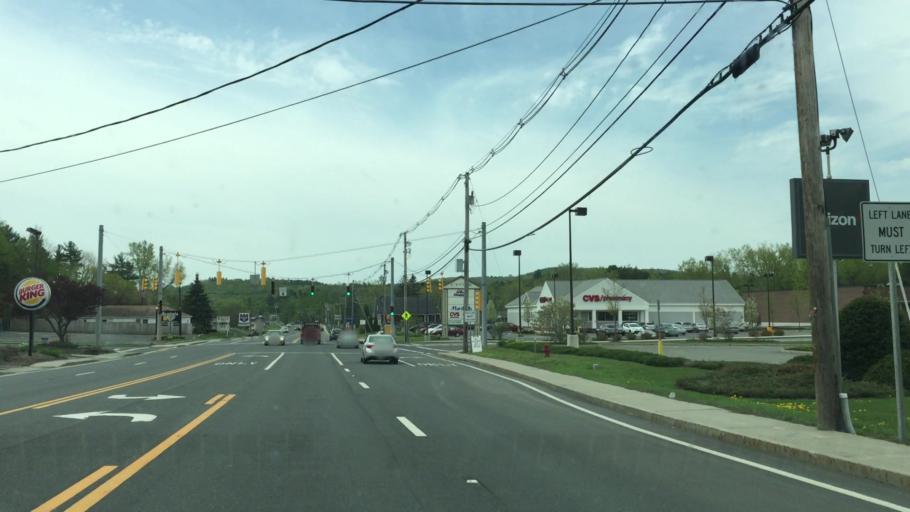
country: US
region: Massachusetts
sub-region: Berkshire County
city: Pittsfield
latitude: 42.4055
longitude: -73.2649
